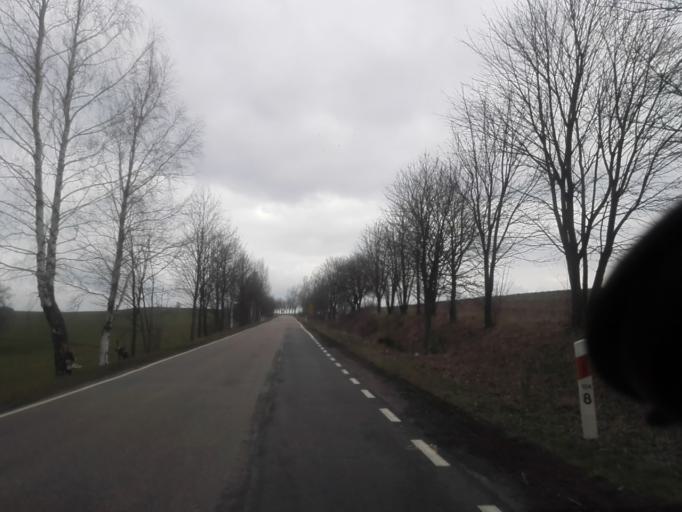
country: PL
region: Podlasie
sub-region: Suwalki
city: Suwalki
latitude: 54.2349
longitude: 22.9139
